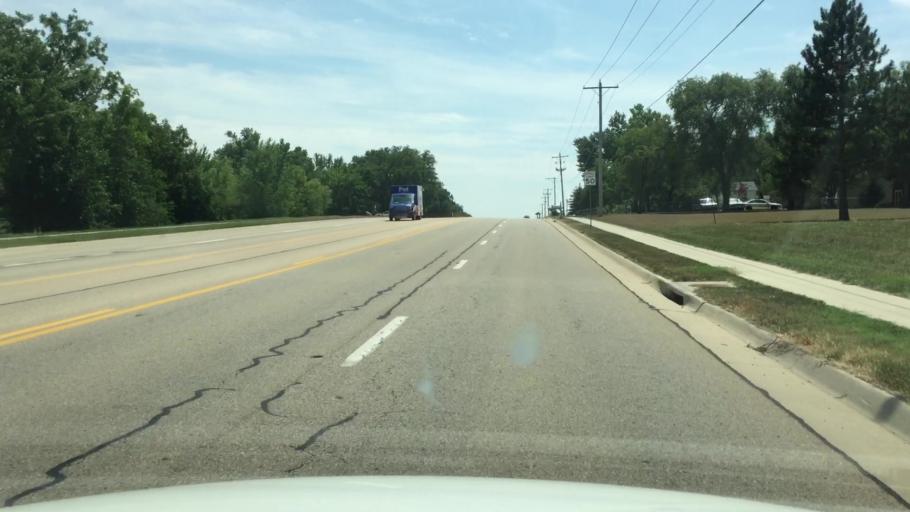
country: US
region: Kansas
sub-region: Shawnee County
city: Topeka
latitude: 39.0001
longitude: -95.6145
